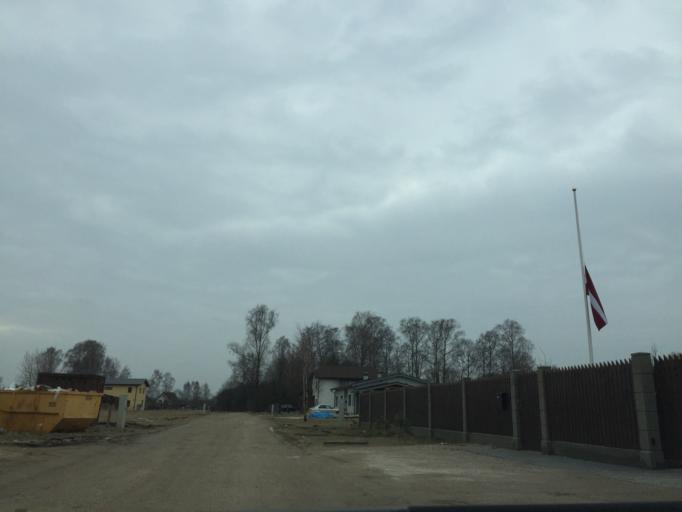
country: LV
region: Marupe
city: Marupe
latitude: 56.8825
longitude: 24.0549
